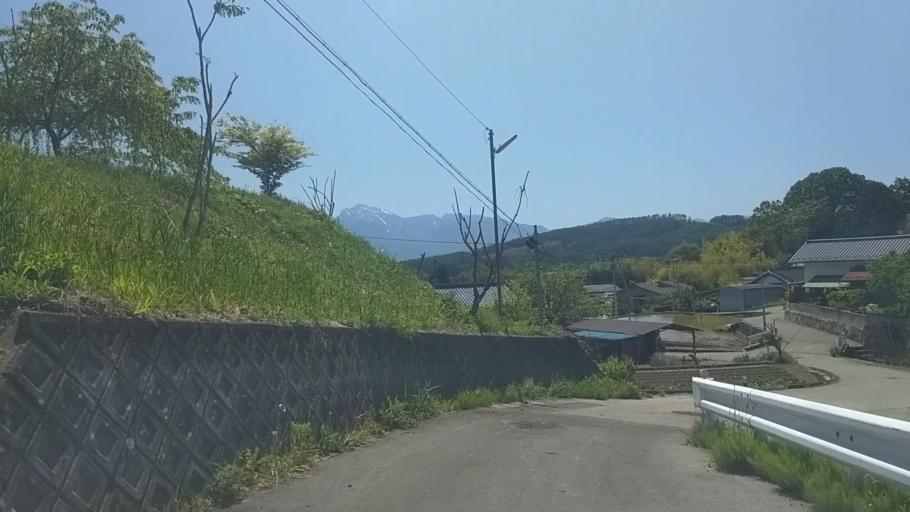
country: JP
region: Yamanashi
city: Nirasaki
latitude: 35.8553
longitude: 138.4490
